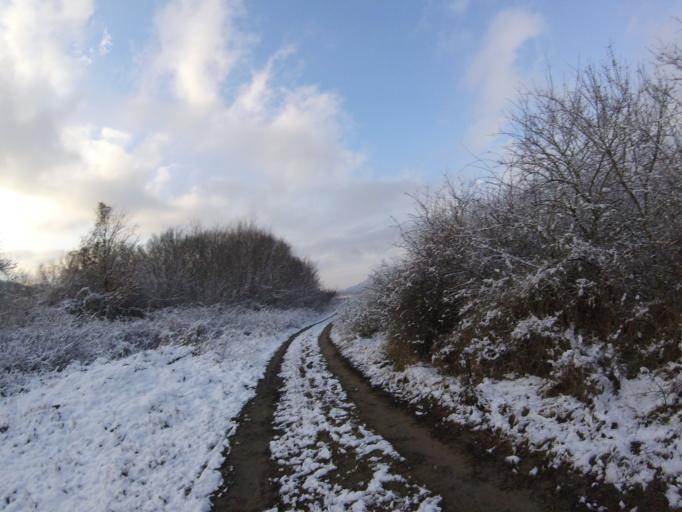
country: HU
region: Komarom-Esztergom
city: Esztergom
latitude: 47.7986
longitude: 18.7970
